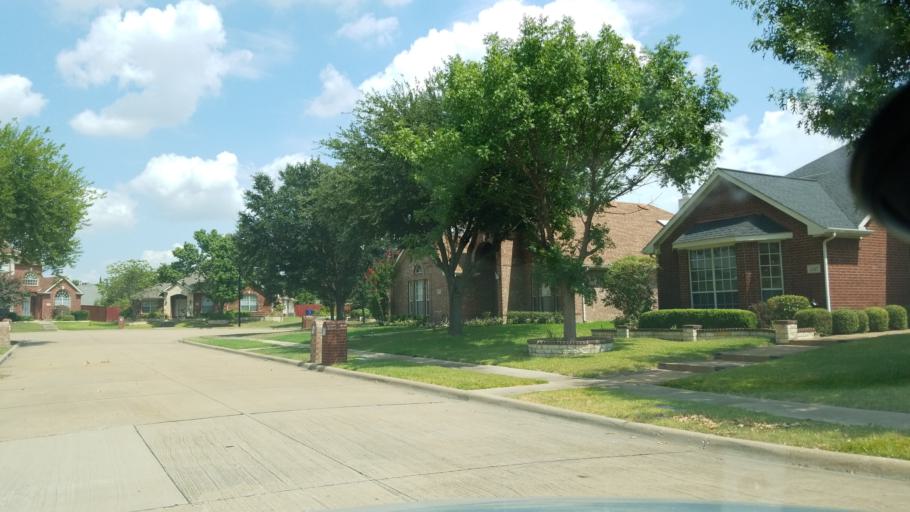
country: US
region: Texas
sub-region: Dallas County
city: Garland
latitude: 32.9250
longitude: -96.6612
